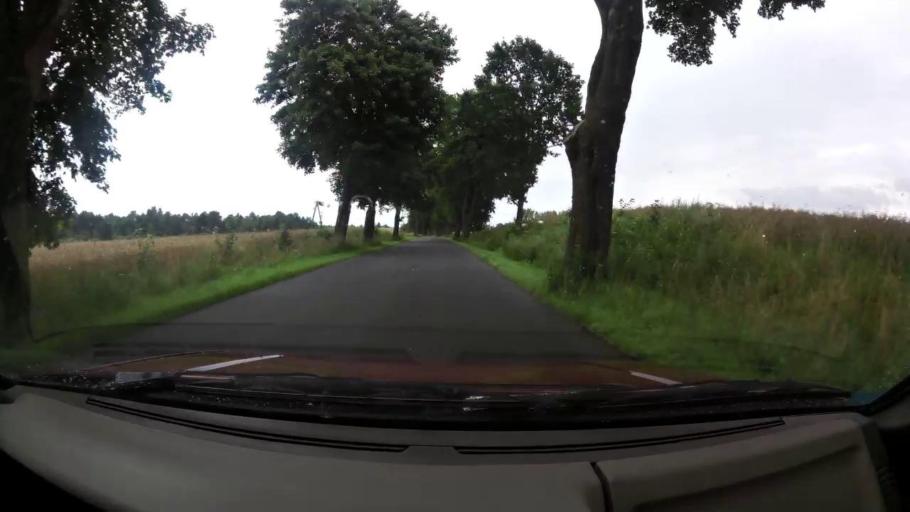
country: PL
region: West Pomeranian Voivodeship
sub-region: Koszalin
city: Koszalin
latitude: 54.1478
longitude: 16.1277
